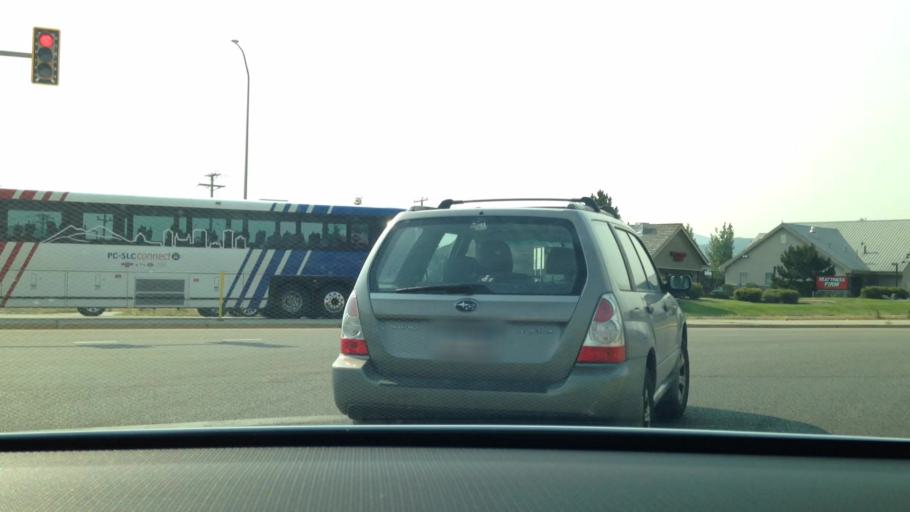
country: US
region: Utah
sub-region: Summit County
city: Snyderville
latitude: 40.7268
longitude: -111.5443
